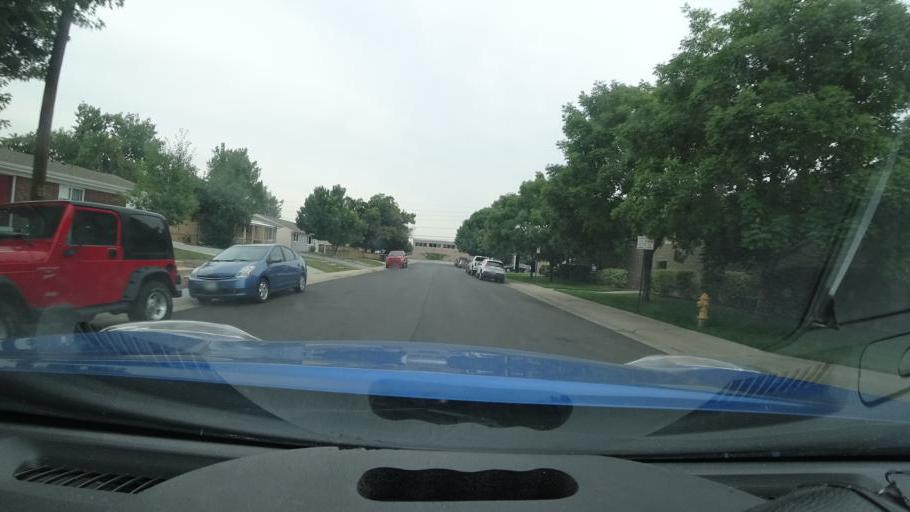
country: US
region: Colorado
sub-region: Arapahoe County
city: Glendale
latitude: 39.6802
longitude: -104.9235
